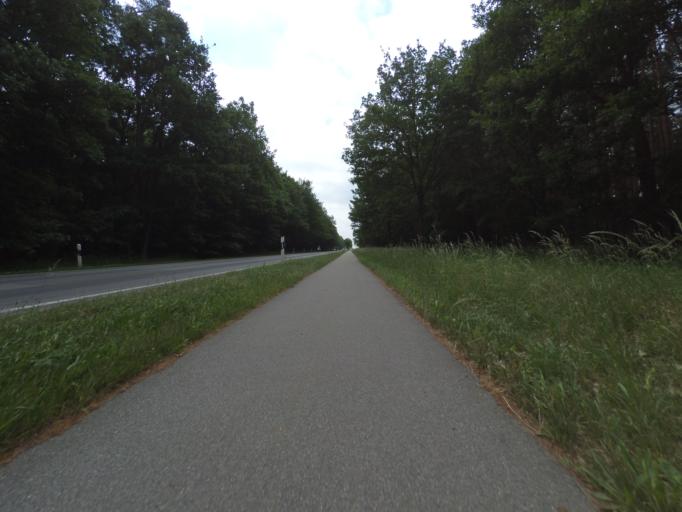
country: DE
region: Mecklenburg-Vorpommern
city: Klink
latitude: 53.4919
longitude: 12.6286
